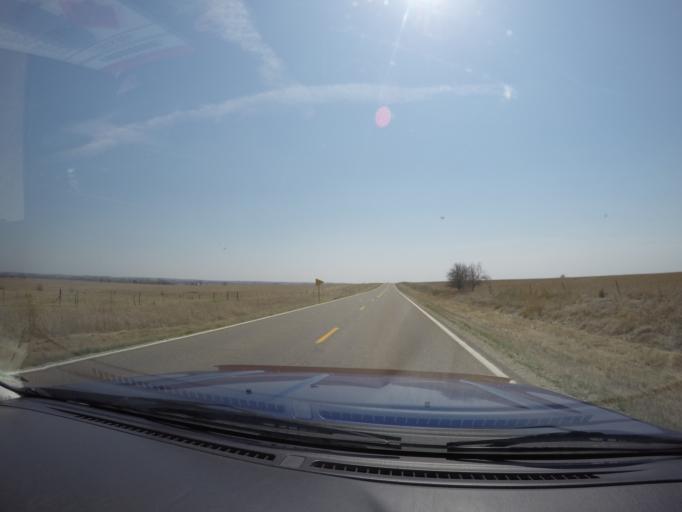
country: US
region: Kansas
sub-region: Morris County
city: Council Grove
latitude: 38.7596
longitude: -96.5011
